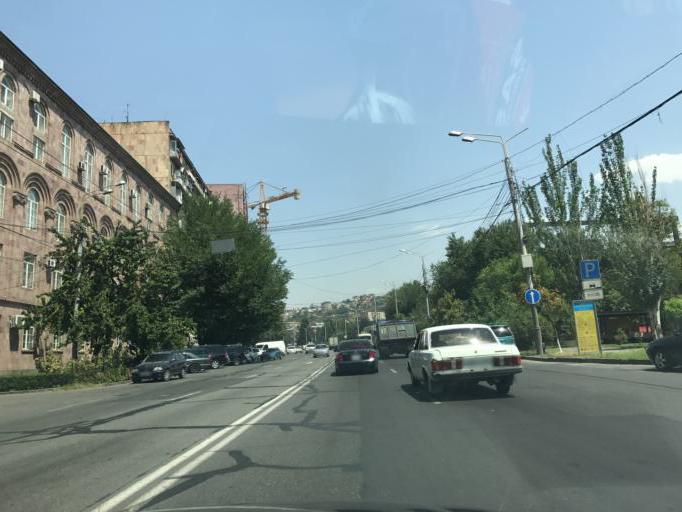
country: AM
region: Yerevan
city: Yerevan
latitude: 40.1751
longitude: 44.5205
